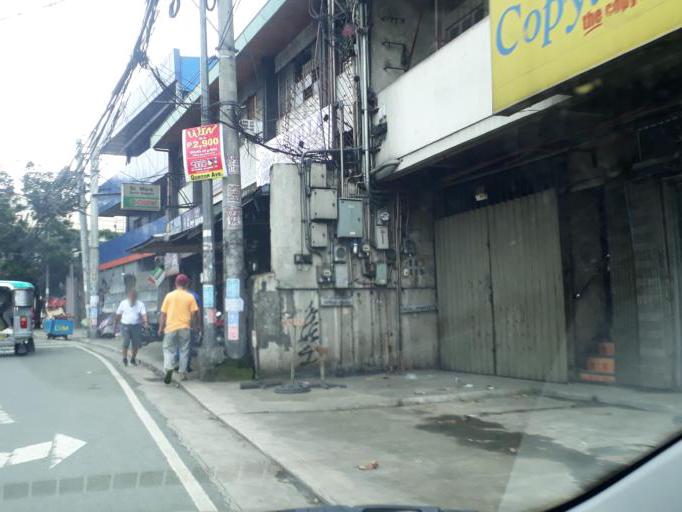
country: PH
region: Calabarzon
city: Del Monte
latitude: 14.6341
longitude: 121.0179
